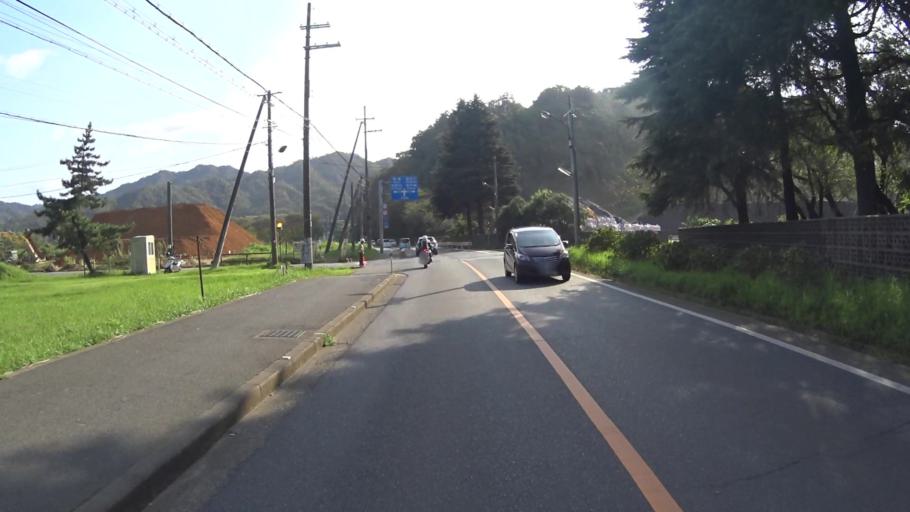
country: JP
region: Kyoto
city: Miyazu
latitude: 35.5565
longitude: 135.1521
